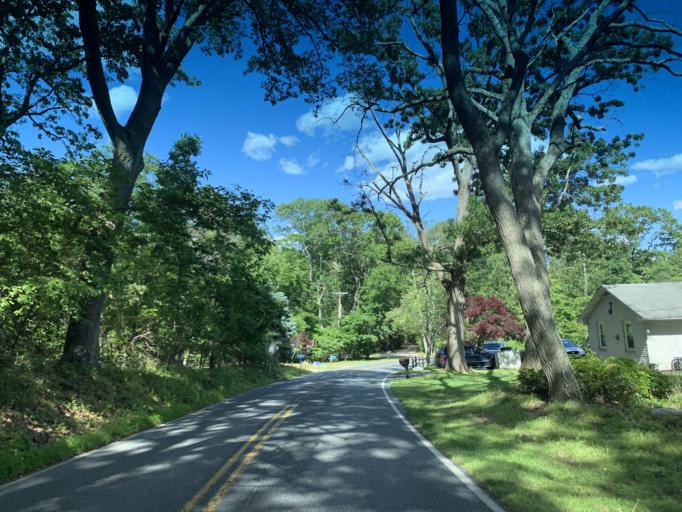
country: US
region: Maryland
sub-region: Cecil County
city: Charlestown
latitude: 39.5460
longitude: -75.9412
